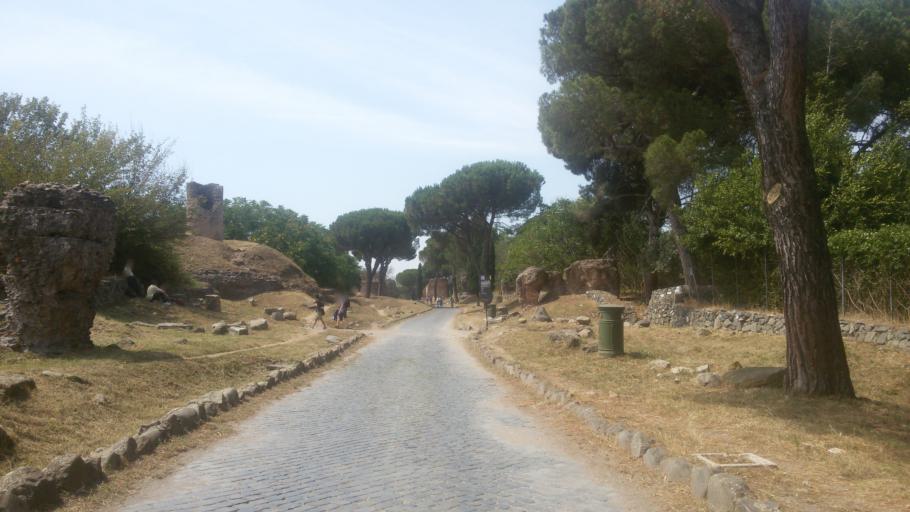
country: IT
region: Latium
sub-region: Citta metropolitana di Roma Capitale
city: Borgo Lotti
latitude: 41.8302
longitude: 12.5452
